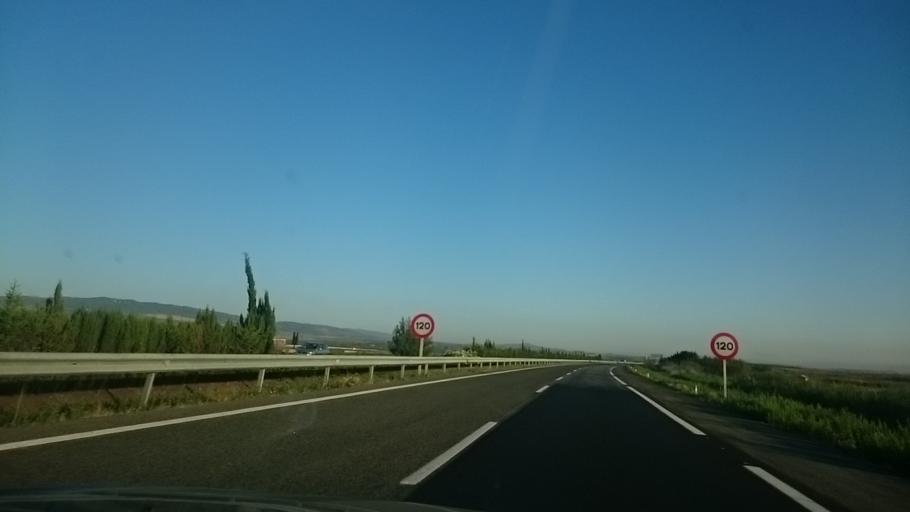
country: ES
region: Navarre
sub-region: Provincia de Navarra
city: Corella
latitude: 42.1379
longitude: -1.7772
